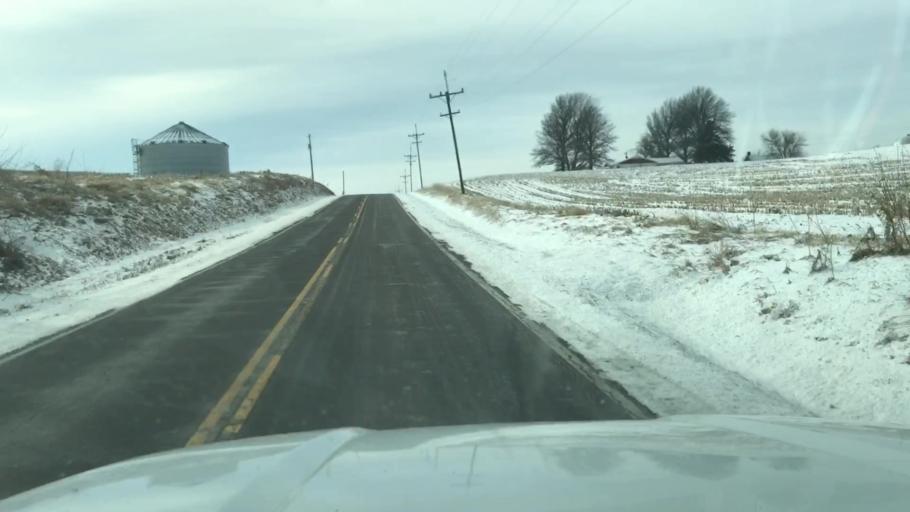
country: US
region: Missouri
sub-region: Holt County
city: Oregon
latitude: 40.0613
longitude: -95.1356
